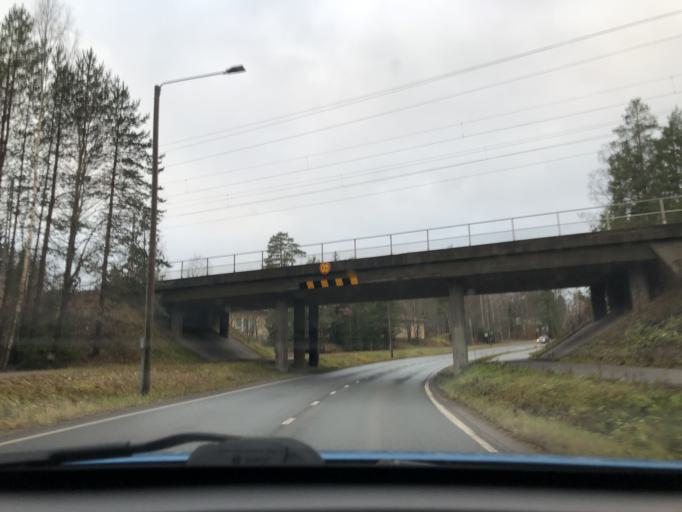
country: FI
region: Pirkanmaa
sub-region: Tampere
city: Kangasala
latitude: 61.5280
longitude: 24.0131
